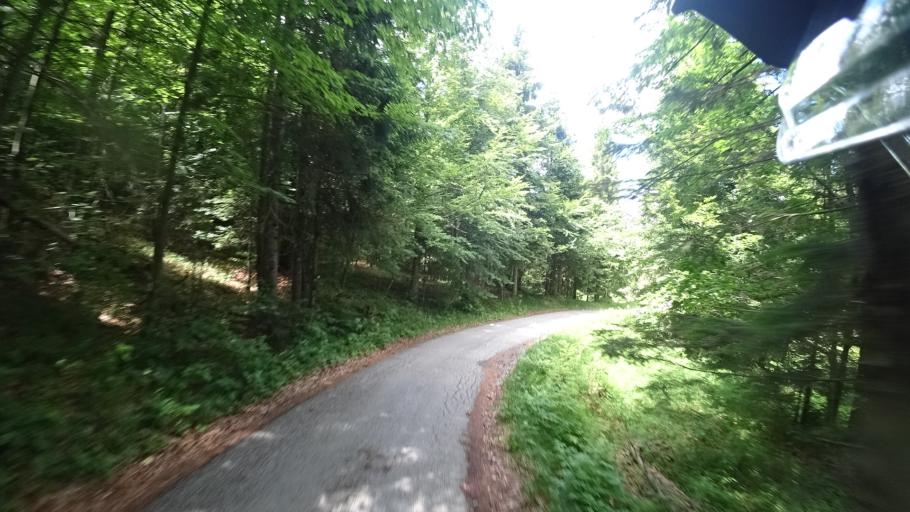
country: SI
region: Loski Potok
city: Hrib-Loski Potok
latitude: 45.6117
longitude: 14.5737
